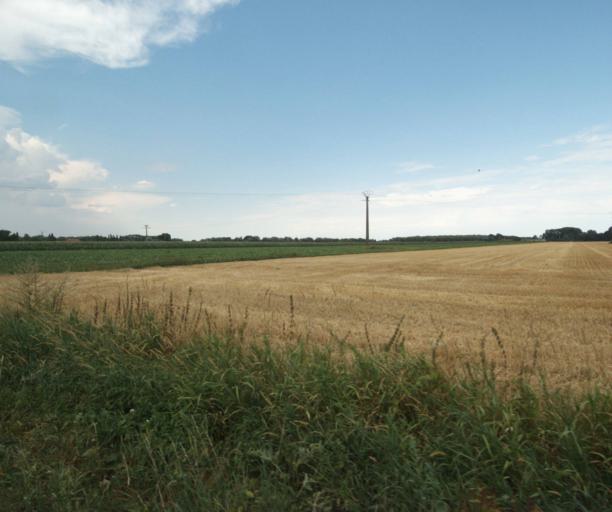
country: FR
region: Nord-Pas-de-Calais
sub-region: Departement du Nord
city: Deulemont
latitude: 50.7440
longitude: 2.9548
